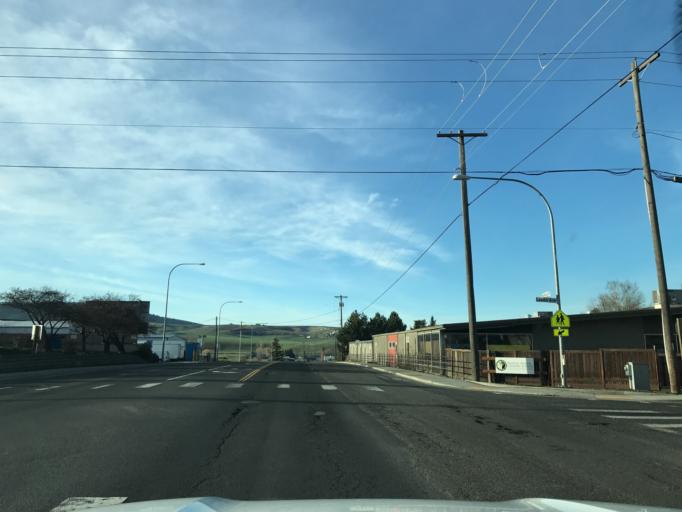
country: US
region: Idaho
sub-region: Latah County
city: Moscow
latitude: 46.7221
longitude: -117.0015
